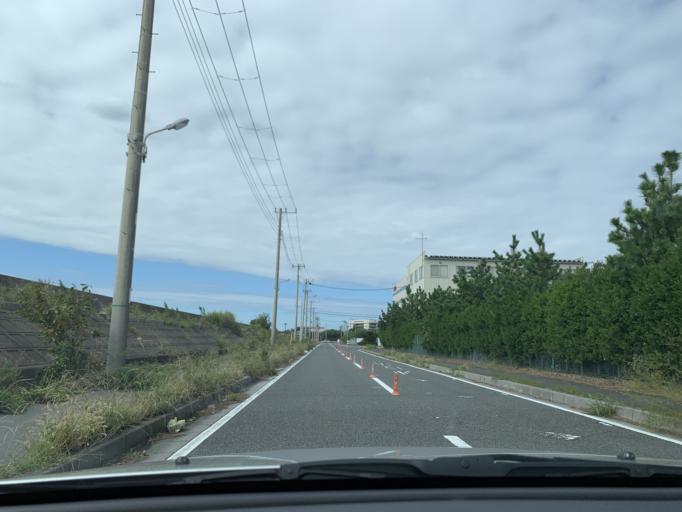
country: JP
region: Tokyo
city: Urayasu
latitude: 35.6201
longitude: 139.8956
